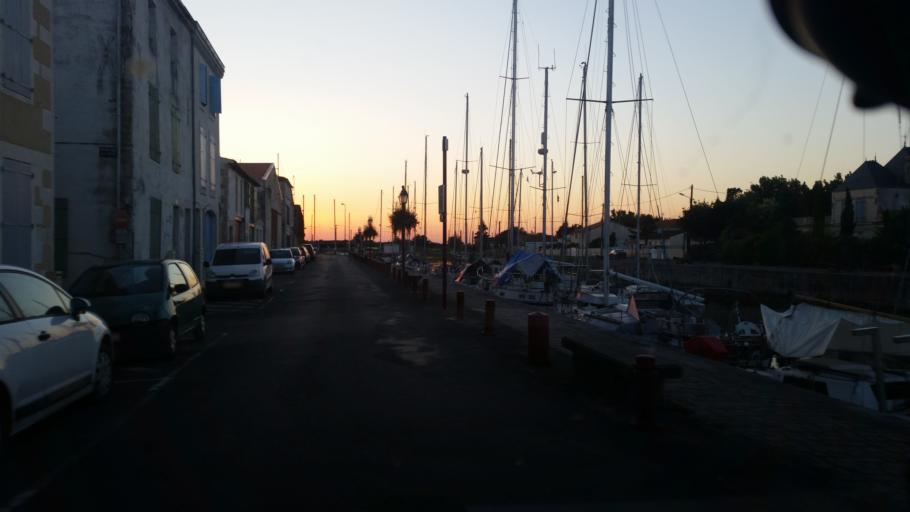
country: FR
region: Poitou-Charentes
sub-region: Departement de la Charente-Maritime
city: Marans
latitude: 46.3121
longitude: -0.9954
